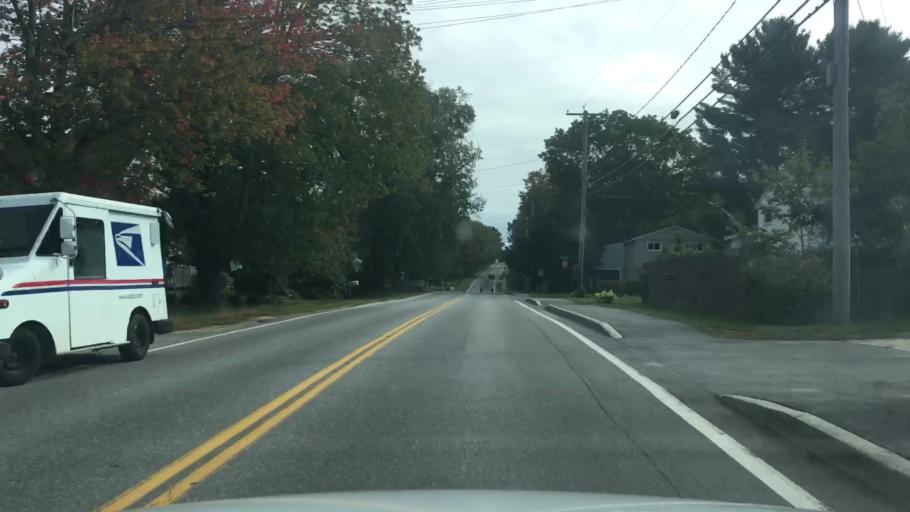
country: US
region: Maine
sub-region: Sagadahoc County
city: Topsham
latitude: 43.9227
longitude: -69.9930
